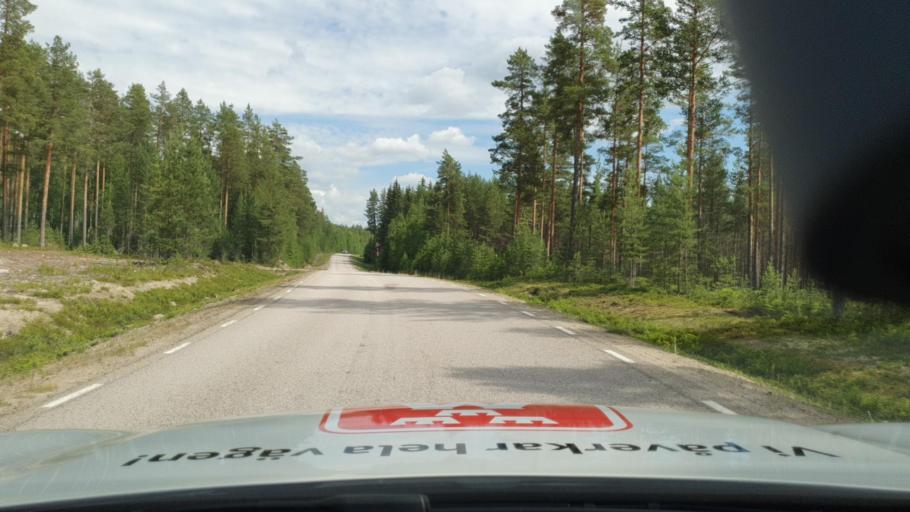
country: NO
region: Hedmark
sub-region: Asnes
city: Flisa
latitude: 60.6980
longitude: 12.5263
